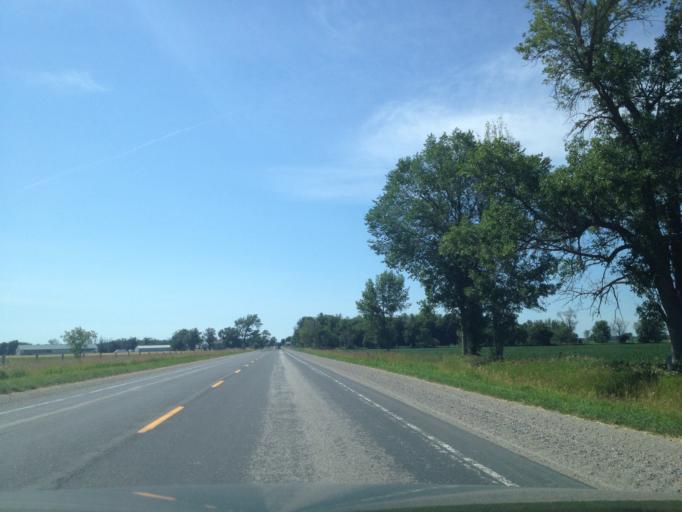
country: CA
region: Ontario
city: Stratford
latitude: 43.4964
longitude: -80.8651
